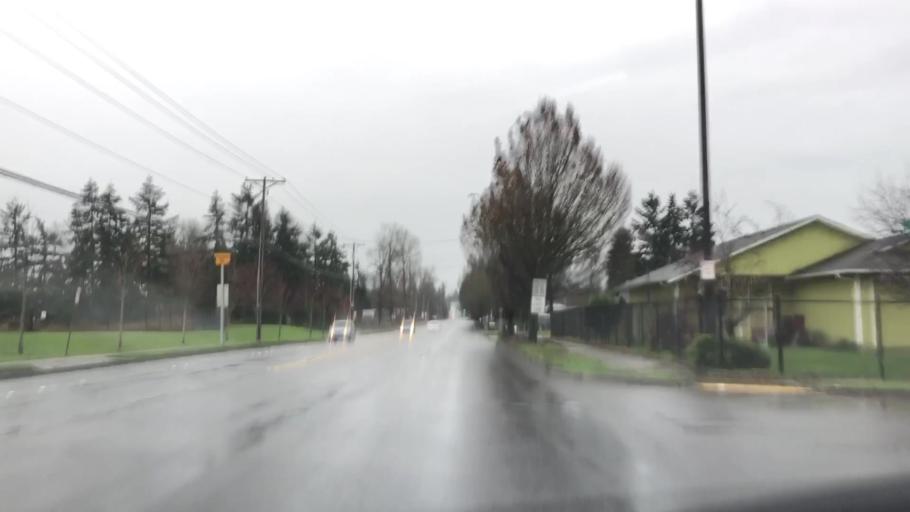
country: US
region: Washington
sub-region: Pierce County
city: Waller
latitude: 47.2099
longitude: -122.4080
